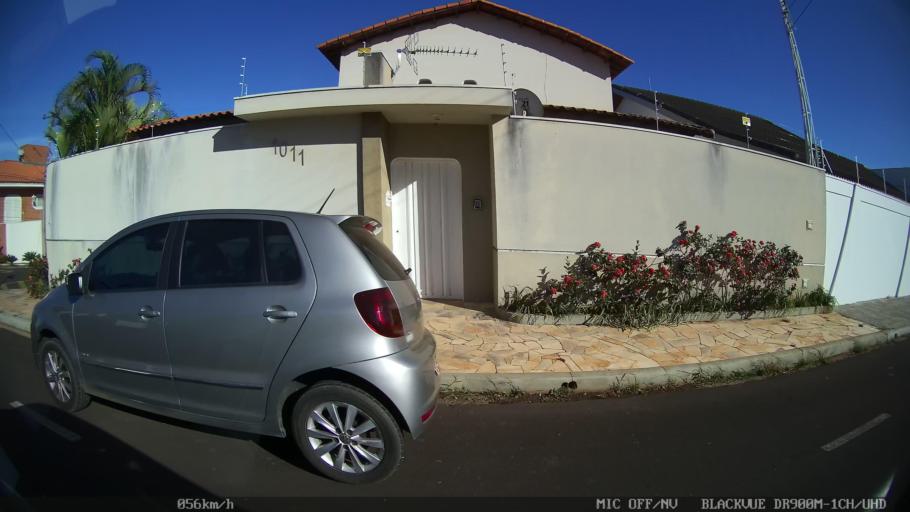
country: BR
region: Sao Paulo
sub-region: Franca
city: Franca
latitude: -20.5445
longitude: -47.4057
